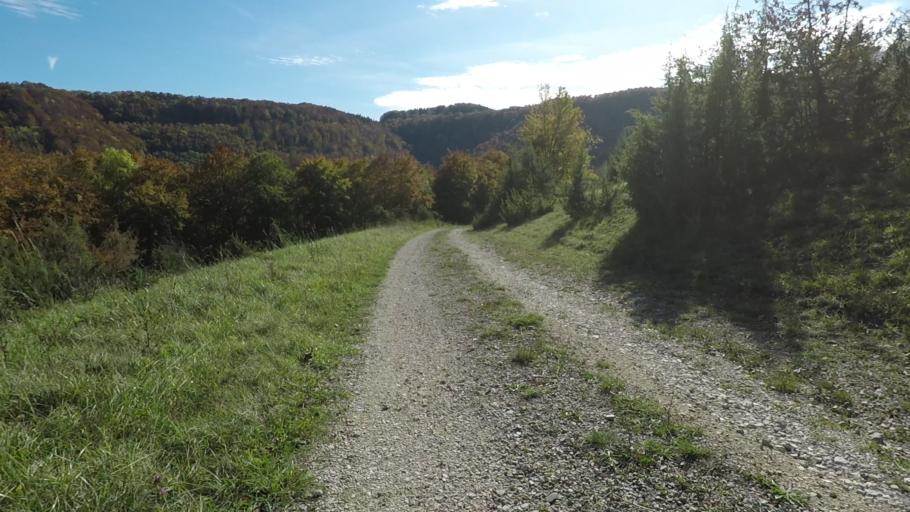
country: DE
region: Baden-Wuerttemberg
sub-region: Tuebingen Region
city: Pfullingen
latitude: 48.4245
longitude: 9.2343
